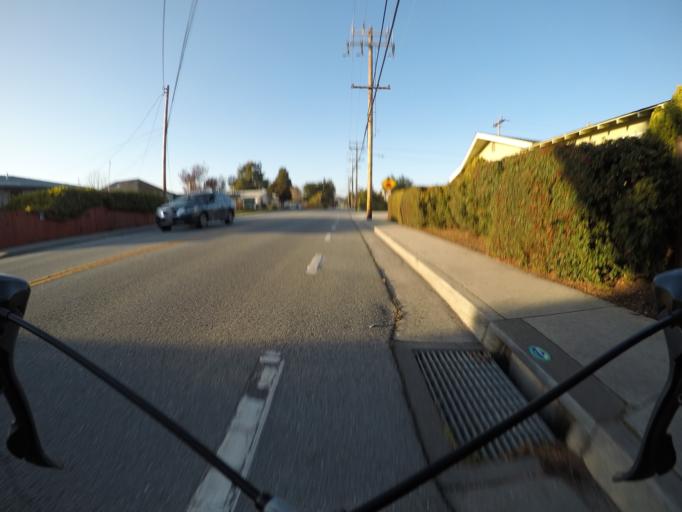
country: US
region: California
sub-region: Santa Cruz County
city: Live Oak
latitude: 36.9810
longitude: -121.9793
